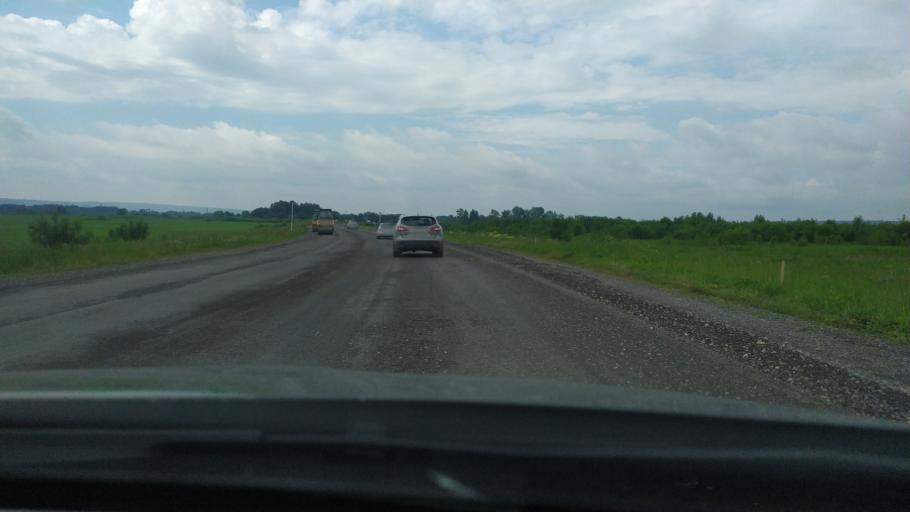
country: RU
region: Perm
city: Kalino
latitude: 58.2920
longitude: 57.4666
